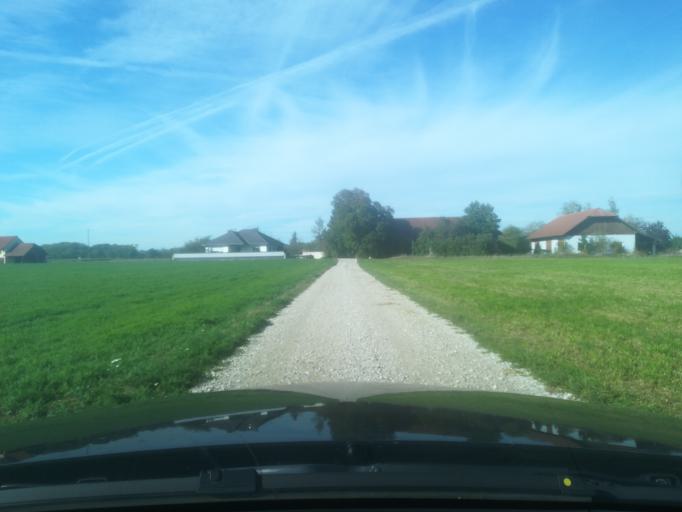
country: AT
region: Upper Austria
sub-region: Politischer Bezirk Linz-Land
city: Horsching
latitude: 48.2064
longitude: 14.1502
